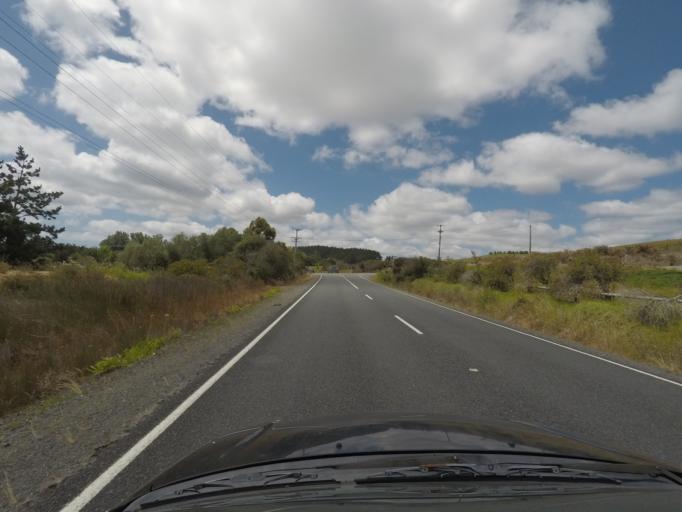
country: NZ
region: Northland
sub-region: Whangarei
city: Ruakaka
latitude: -36.0132
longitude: 174.4833
